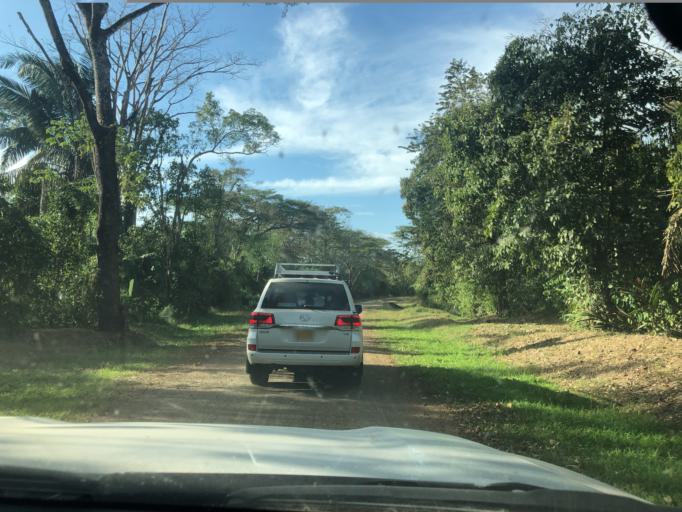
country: CR
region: Alajuela
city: San Jose
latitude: 11.1124
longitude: -85.2820
